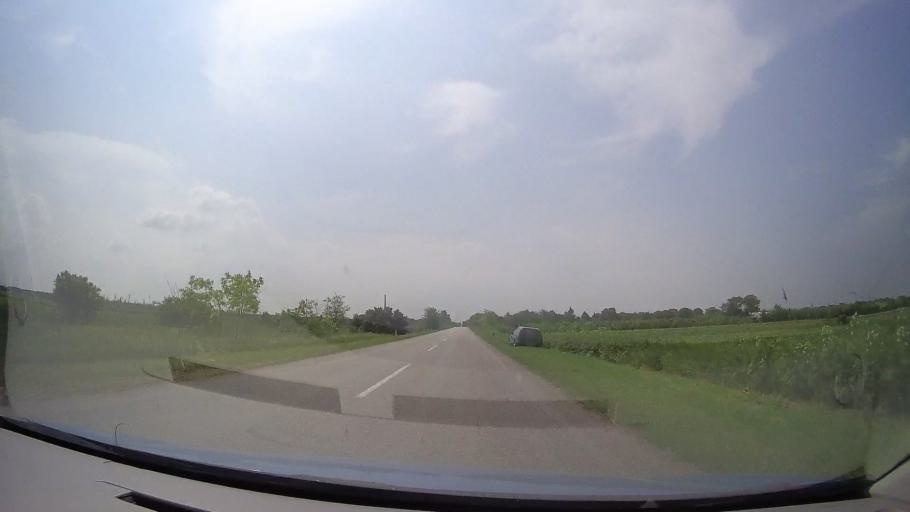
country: RS
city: Crepaja
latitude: 44.9508
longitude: 20.6635
